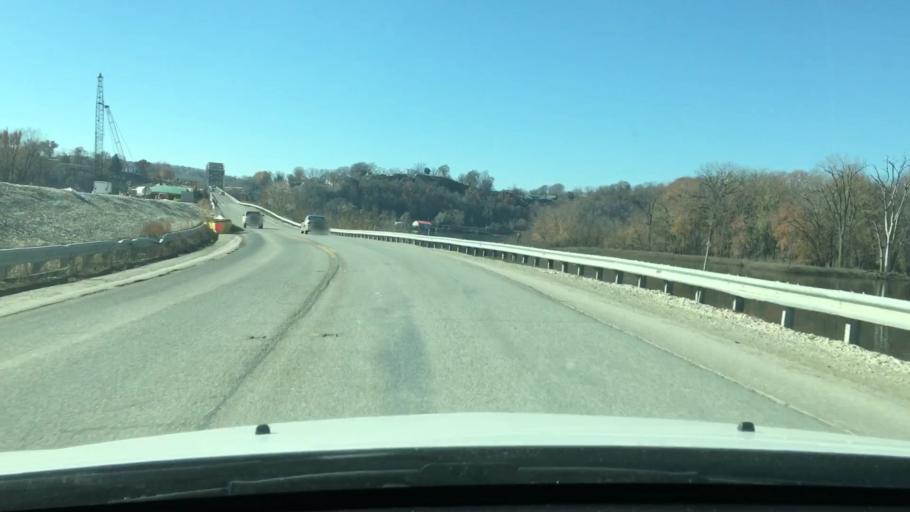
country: US
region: Missouri
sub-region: Pike County
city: Louisiana
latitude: 39.4599
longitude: -91.0412
